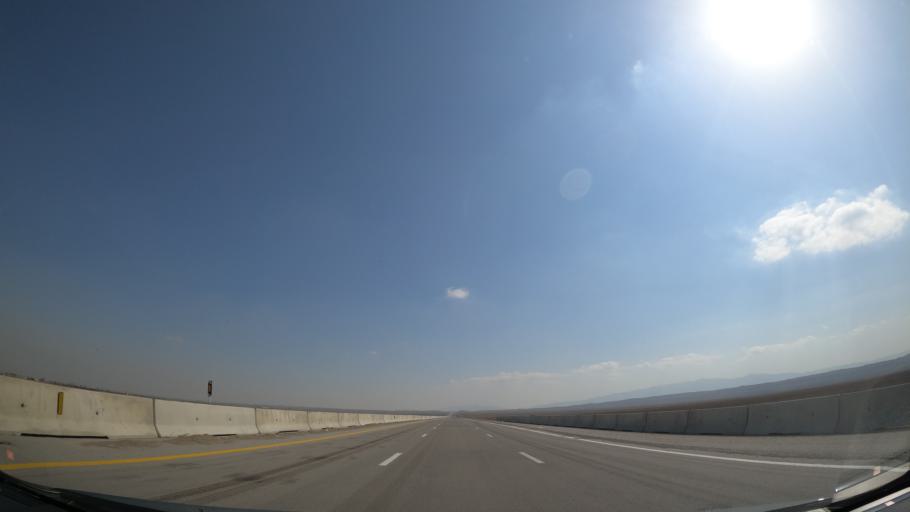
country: IR
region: Alborz
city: Nazarabad
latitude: 35.8362
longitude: 50.4930
